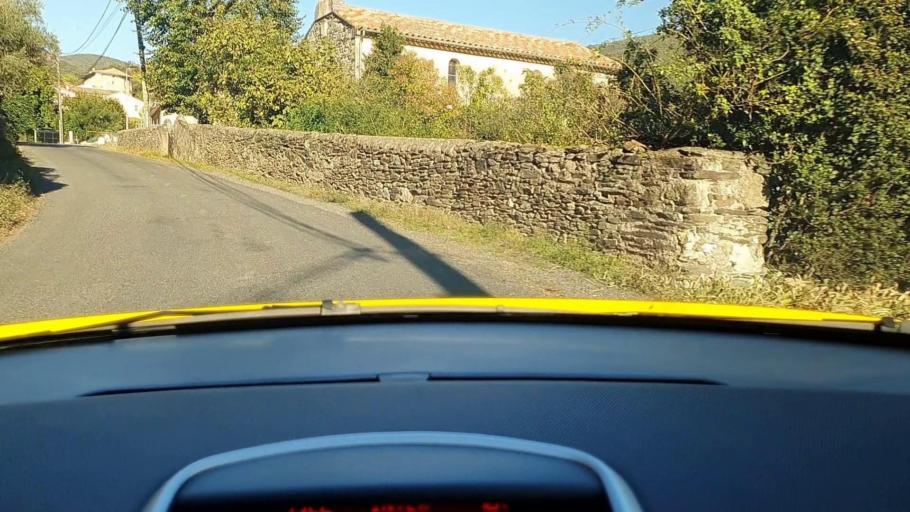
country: FR
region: Languedoc-Roussillon
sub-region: Departement du Gard
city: Sumene
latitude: 44.0068
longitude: 3.7119
